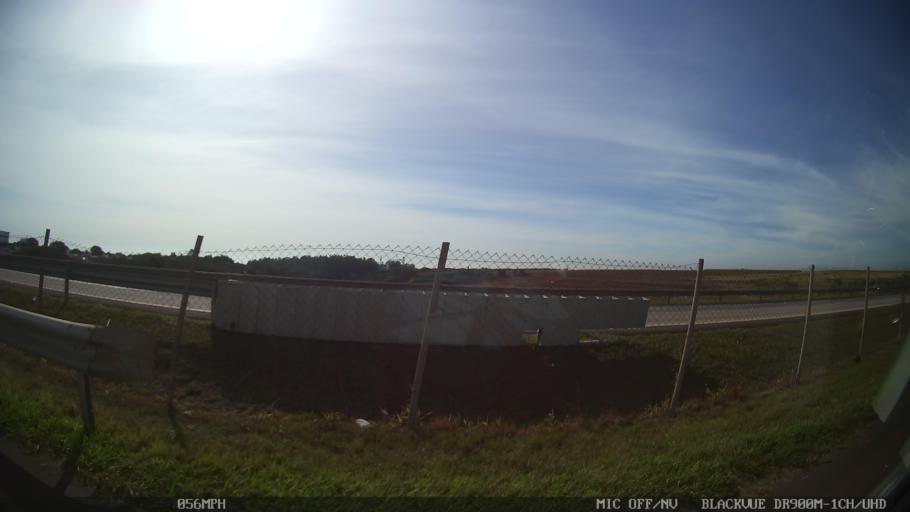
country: BR
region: Sao Paulo
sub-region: Rio Das Pedras
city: Rio das Pedras
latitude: -22.7767
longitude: -47.5905
